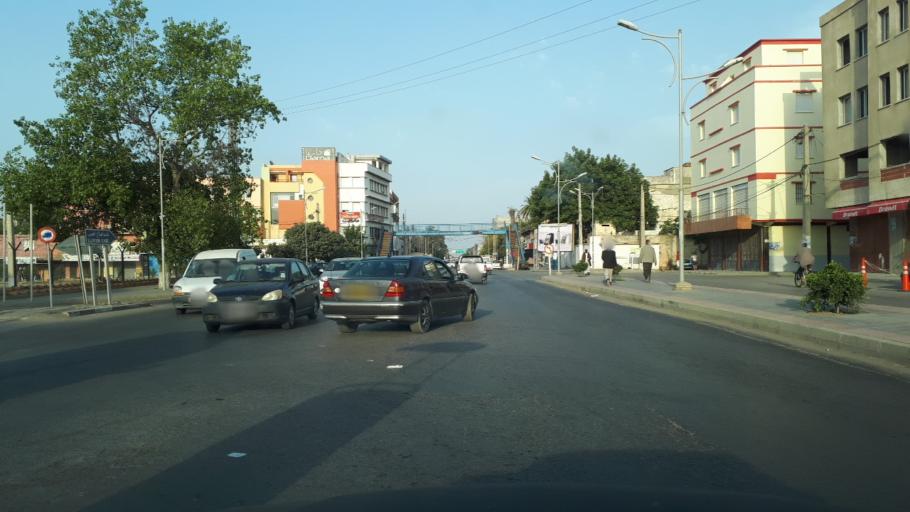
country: DZ
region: Alger
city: Dar el Beida
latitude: 36.7305
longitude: 3.2362
